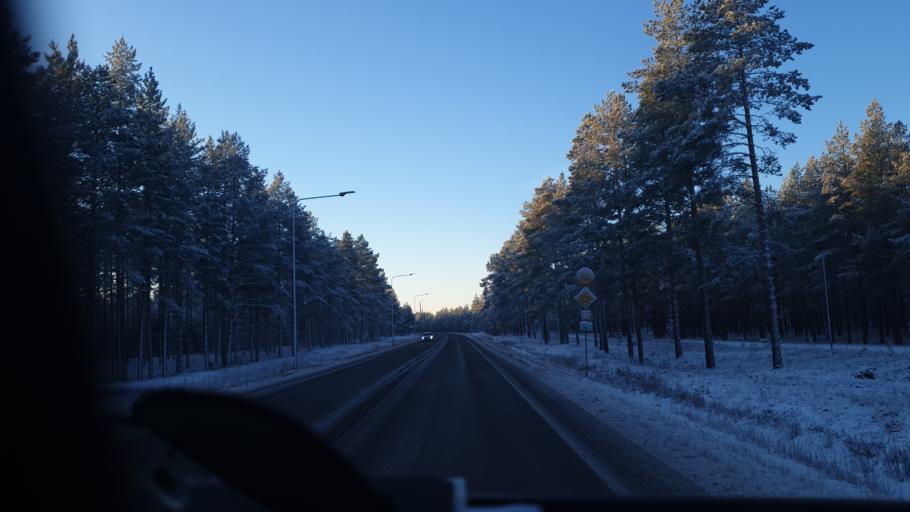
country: FI
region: Northern Ostrobothnia
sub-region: Ylivieska
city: Kalajoki
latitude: 64.2400
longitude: 23.8423
